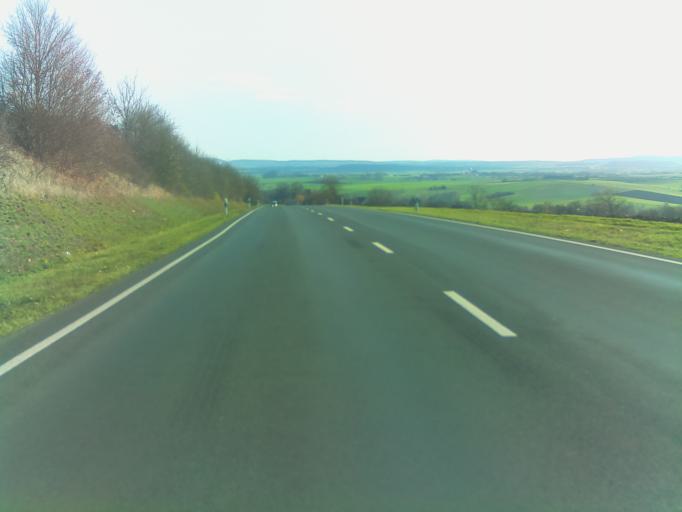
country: DE
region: Bavaria
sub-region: Regierungsbezirk Unterfranken
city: Grosseibstadt
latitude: 50.3055
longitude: 10.3954
